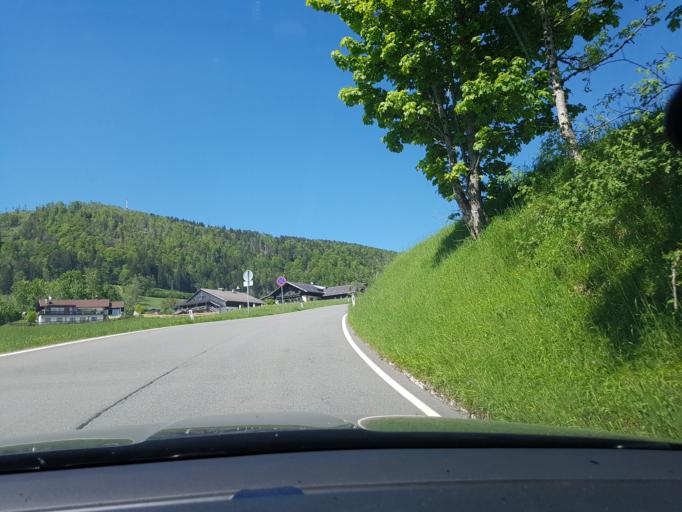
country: AT
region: Salzburg
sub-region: Politischer Bezirk Salzburg-Umgebung
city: Koppl
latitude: 47.7932
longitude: 13.1140
